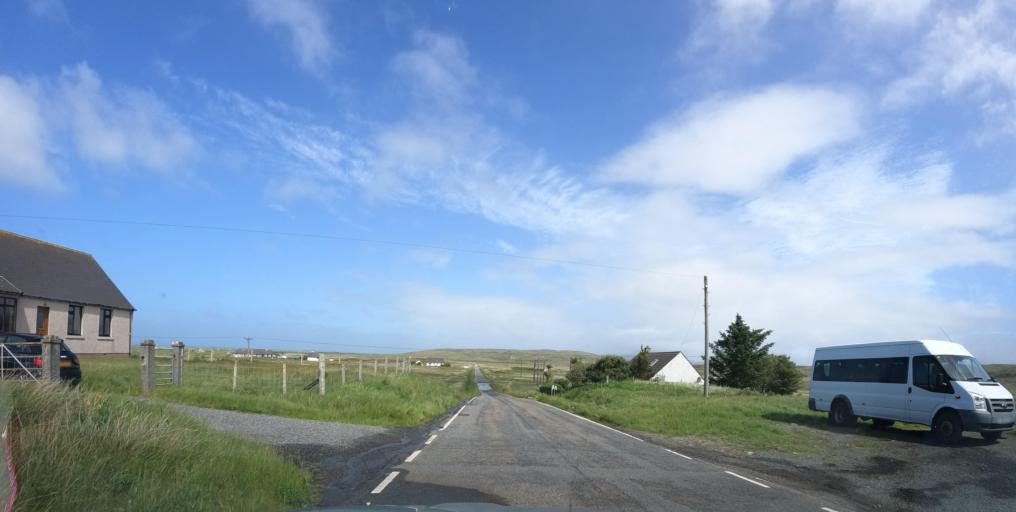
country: GB
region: Scotland
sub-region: Eilean Siar
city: Isle of South Uist
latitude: 57.1262
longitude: -7.3600
